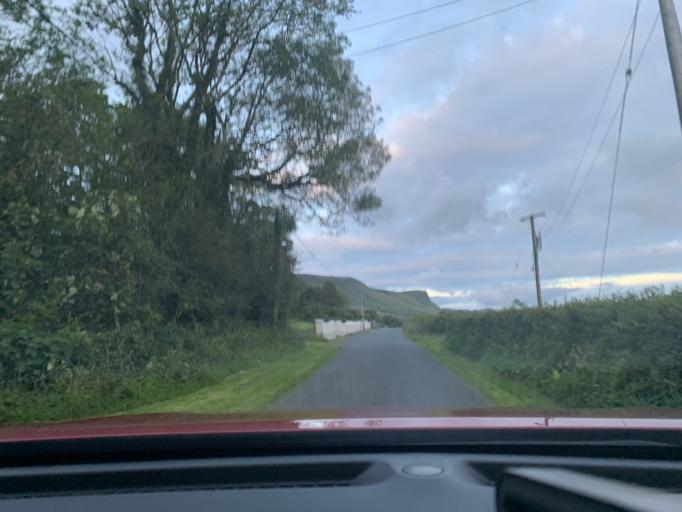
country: IE
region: Connaught
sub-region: Sligo
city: Sligo
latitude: 54.3578
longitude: -8.5036
